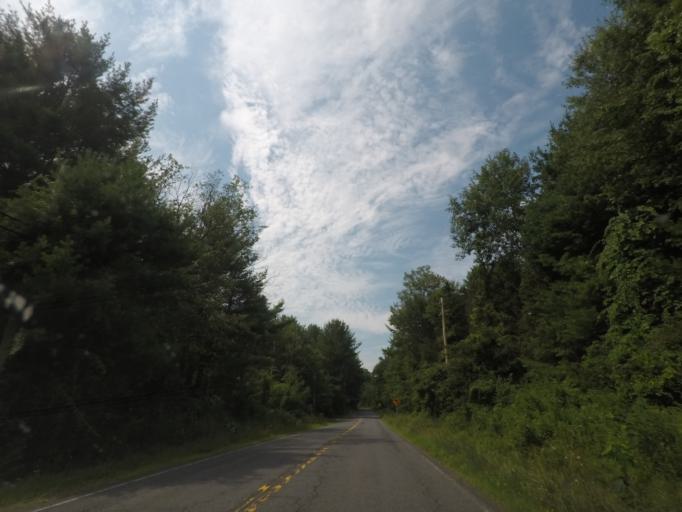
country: US
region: New York
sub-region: Rensselaer County
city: Wynantskill
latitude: 42.7445
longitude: -73.6056
